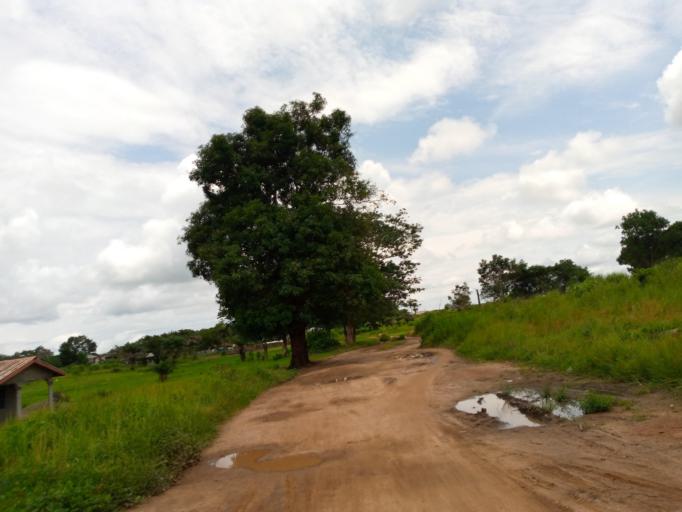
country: SL
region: Northern Province
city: Magburaka
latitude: 8.7112
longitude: -11.9625
